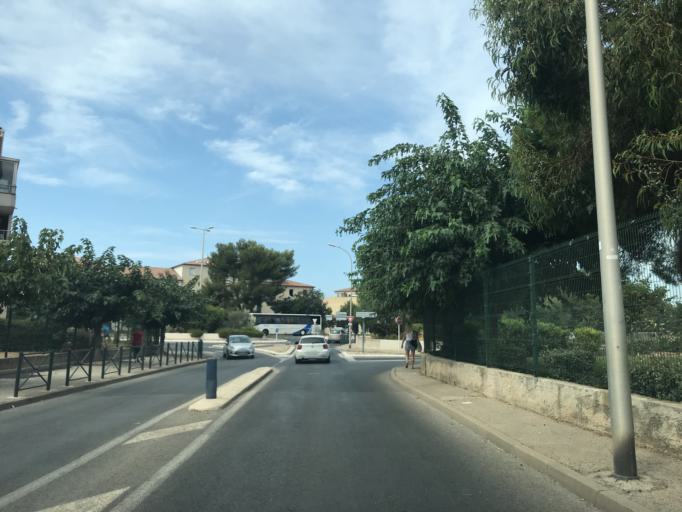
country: FR
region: Provence-Alpes-Cote d'Azur
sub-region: Departement du Var
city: Six-Fours-les-Plages
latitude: 43.0986
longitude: 5.8217
